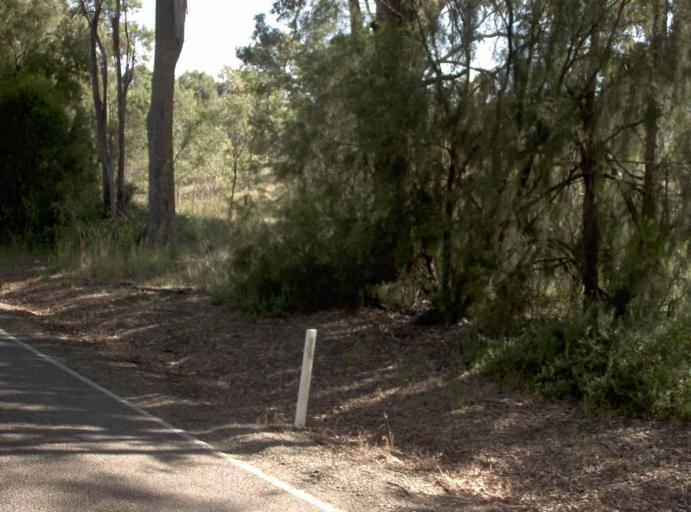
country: AU
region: Victoria
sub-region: East Gippsland
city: Lakes Entrance
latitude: -37.7919
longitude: 147.8306
